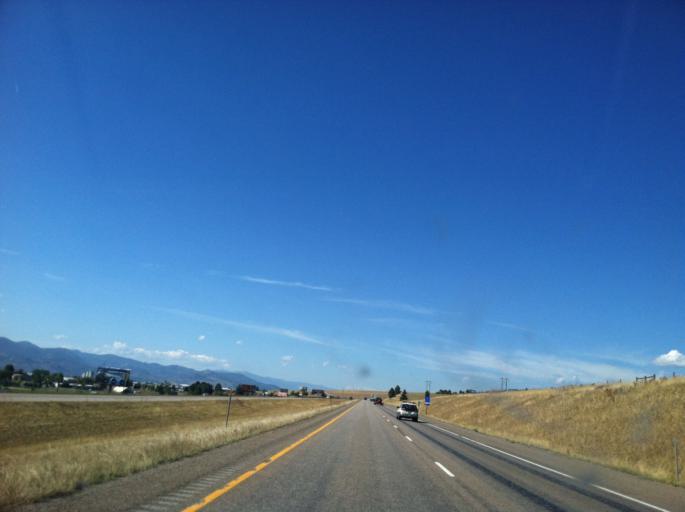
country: US
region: Montana
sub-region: Missoula County
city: Orchard Homes
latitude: 46.9306
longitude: -114.0824
